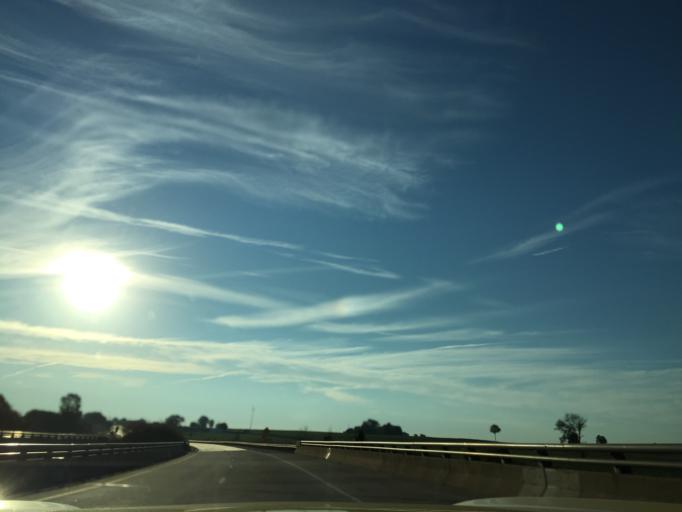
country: US
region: Pennsylvania
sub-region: Berks County
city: Kutztown
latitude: 40.5312
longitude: -75.7614
